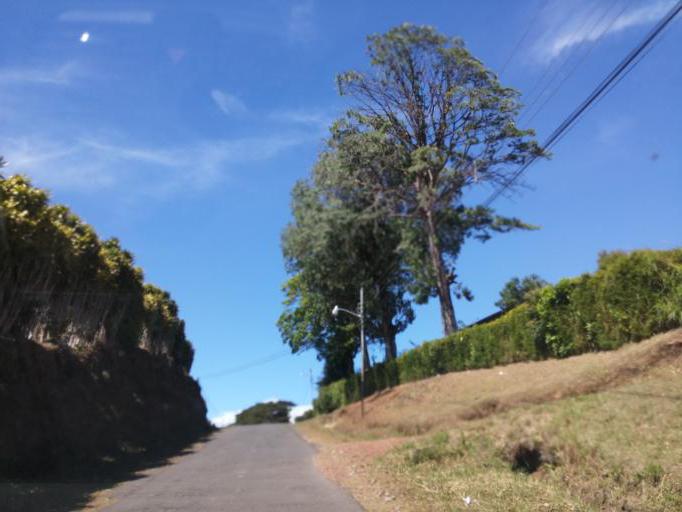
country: CR
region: Alajuela
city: Sabanilla
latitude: 10.0991
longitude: -84.1855
